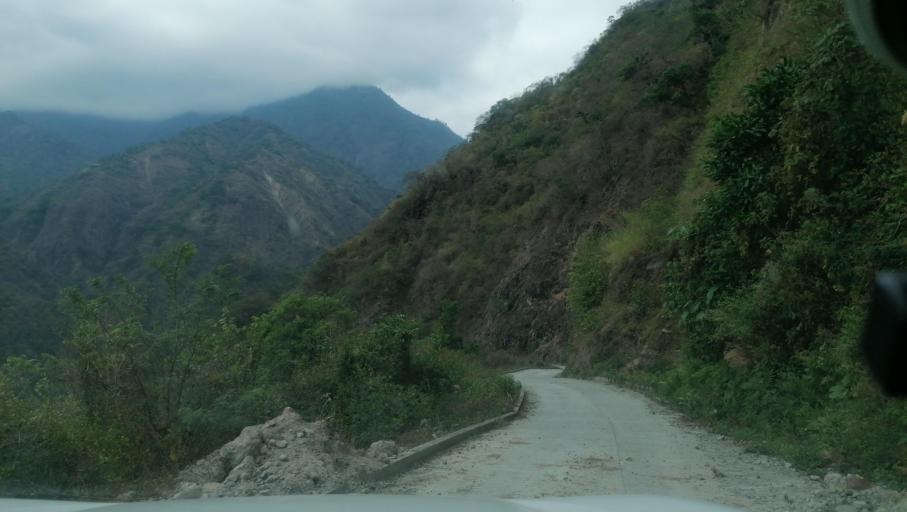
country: MX
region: Chiapas
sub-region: Cacahoatan
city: Benito Juarez
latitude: 15.1608
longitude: -92.1755
